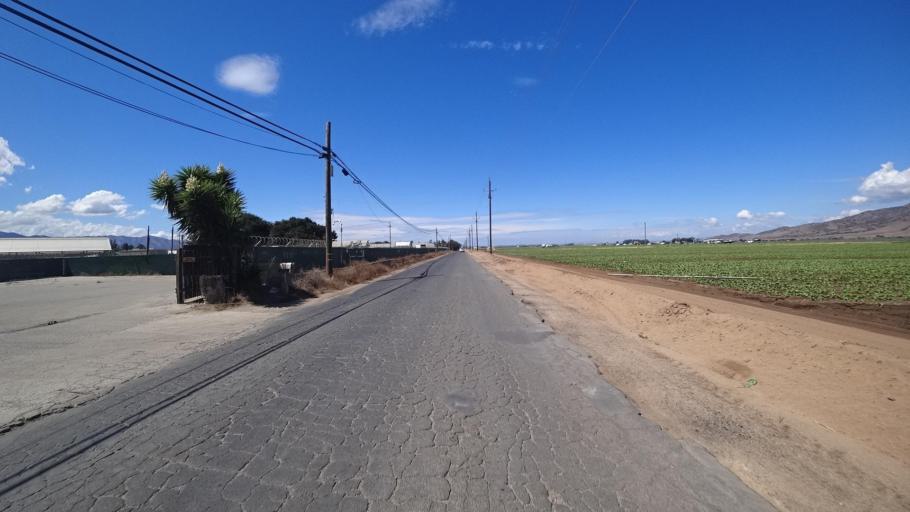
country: US
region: California
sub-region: Monterey County
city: Chualar
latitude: 36.6220
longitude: -121.5131
